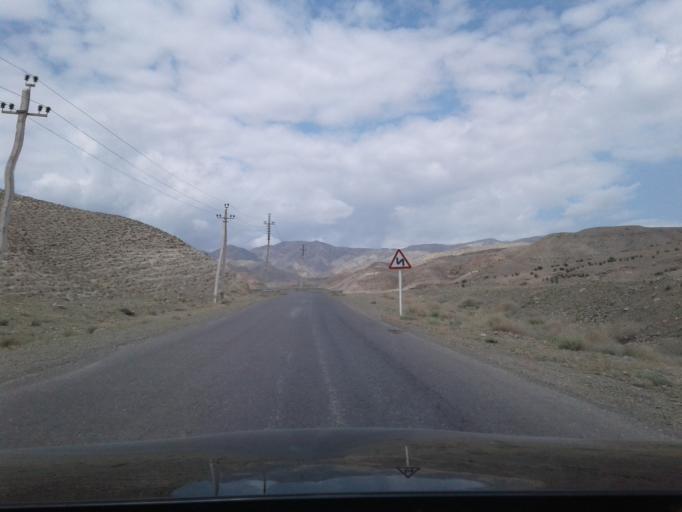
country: TM
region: Ahal
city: Baharly
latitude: 38.5010
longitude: 57.1139
